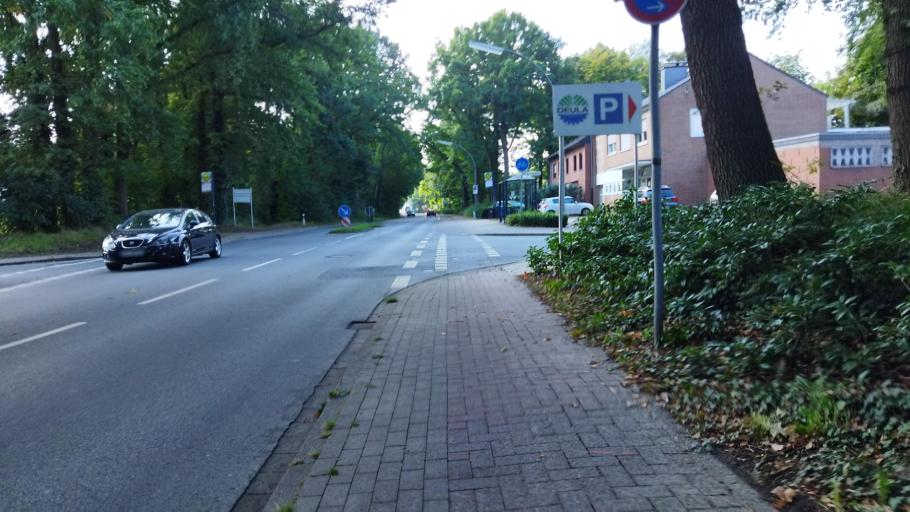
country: DE
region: North Rhine-Westphalia
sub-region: Regierungsbezirk Munster
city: Warendorf
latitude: 51.9718
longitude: 7.9936
